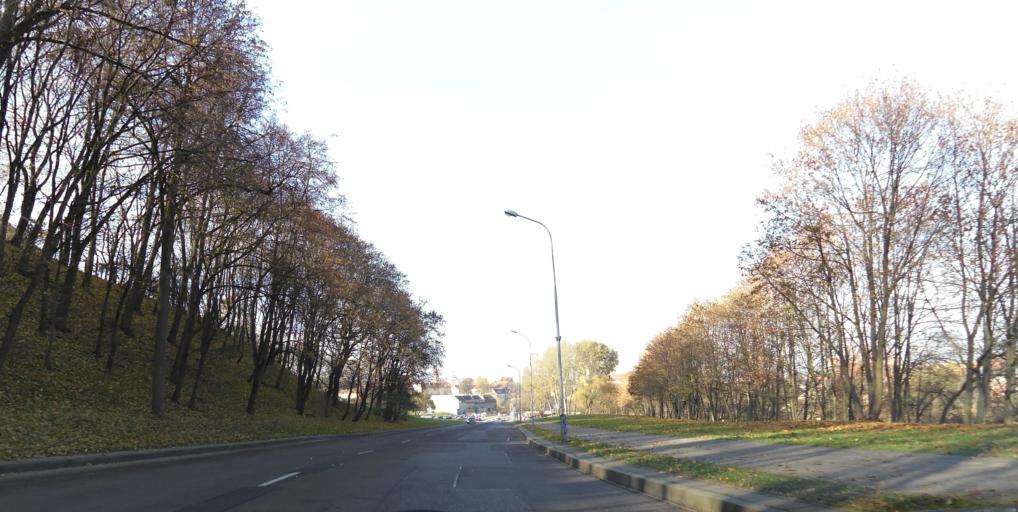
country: LT
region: Vilnius County
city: Rasos
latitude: 54.6774
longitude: 25.2978
